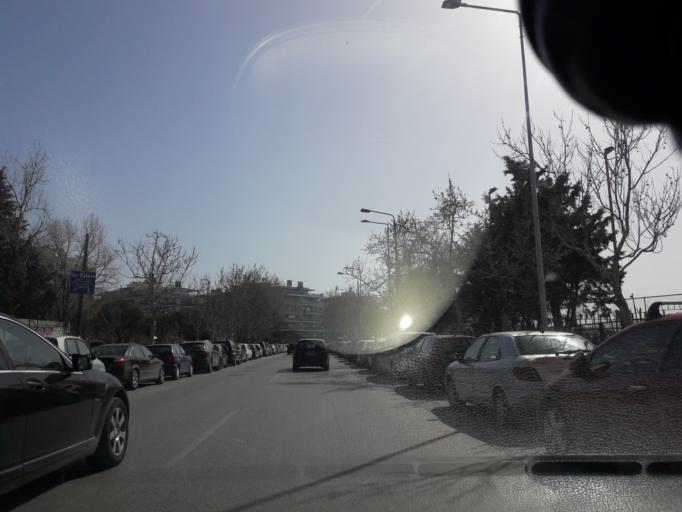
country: GR
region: Central Macedonia
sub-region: Nomos Thessalonikis
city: Kalamaria
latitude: 40.5960
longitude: 22.9503
